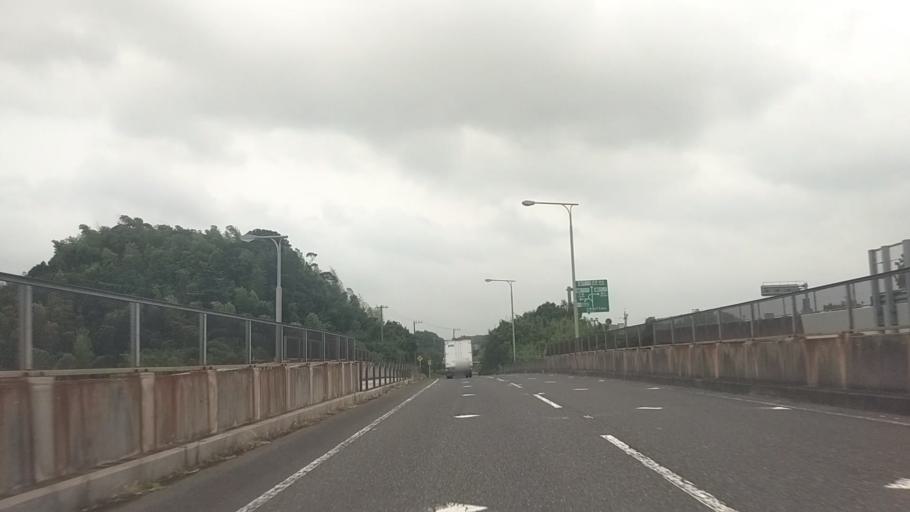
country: JP
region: Chiba
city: Kisarazu
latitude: 35.3916
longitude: 139.9699
